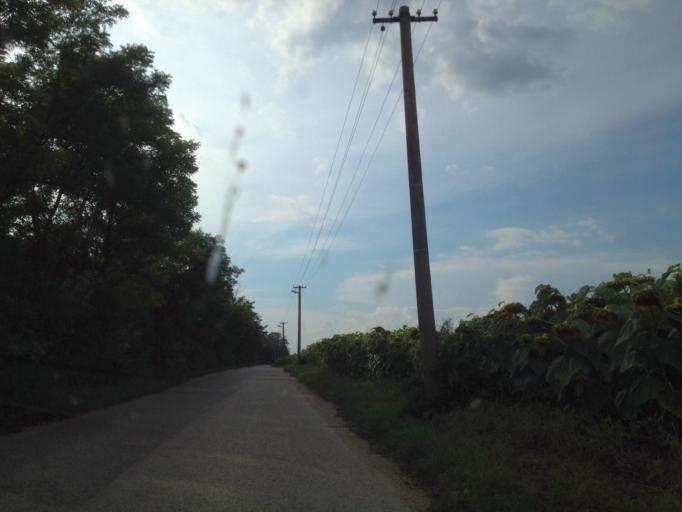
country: SK
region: Nitriansky
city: Svodin
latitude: 47.8982
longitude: 18.4041
